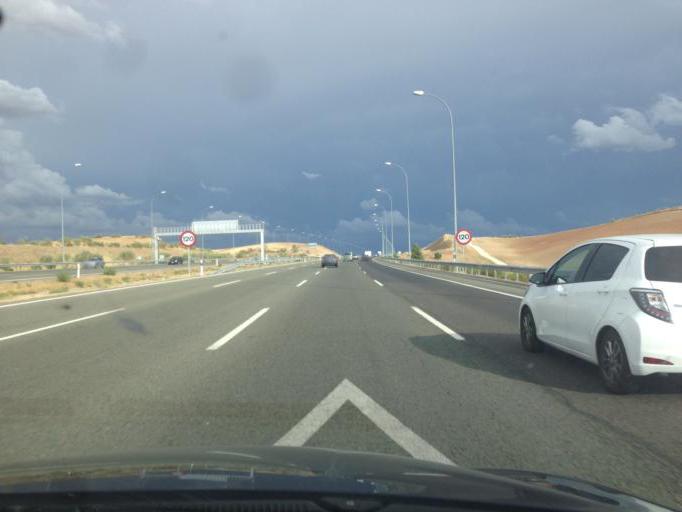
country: ES
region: Madrid
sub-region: Provincia de Madrid
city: Paracuellos de Jarama
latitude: 40.5376
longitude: -3.5285
